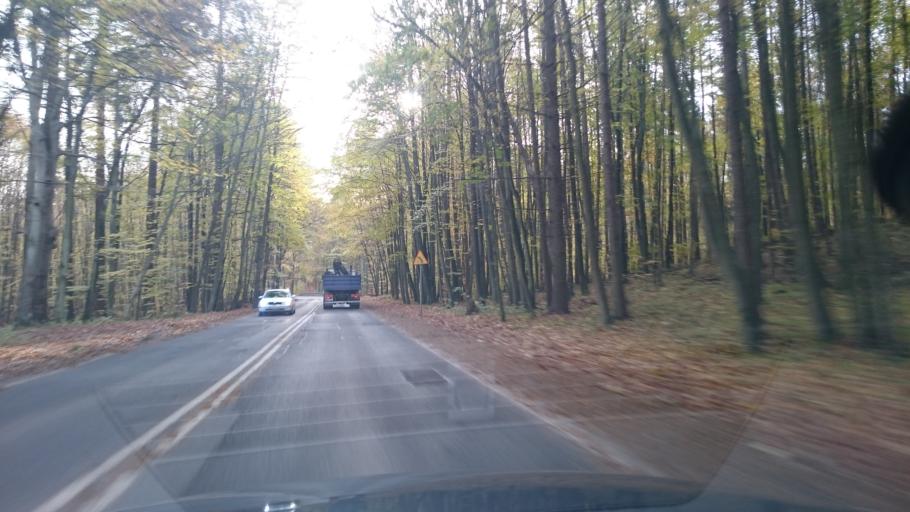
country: PL
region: Pomeranian Voivodeship
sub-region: Gdynia
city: Wielki Kack
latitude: 54.4571
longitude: 18.5138
